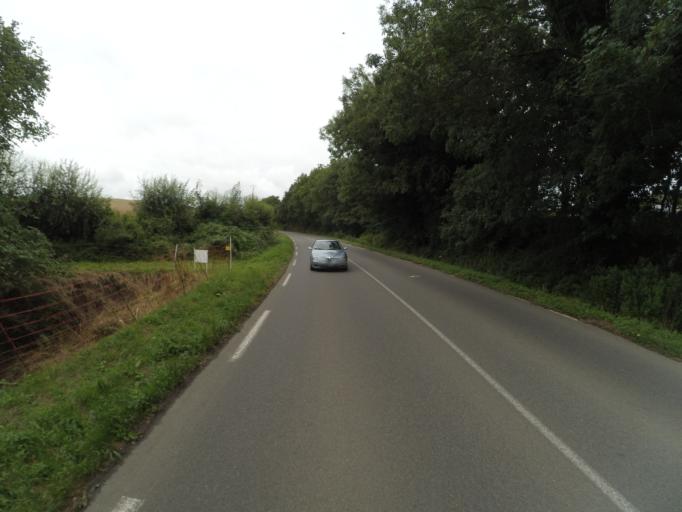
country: FR
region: Brittany
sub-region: Departement des Cotes-d'Armor
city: Tremuson
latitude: 48.5227
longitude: -2.8414
